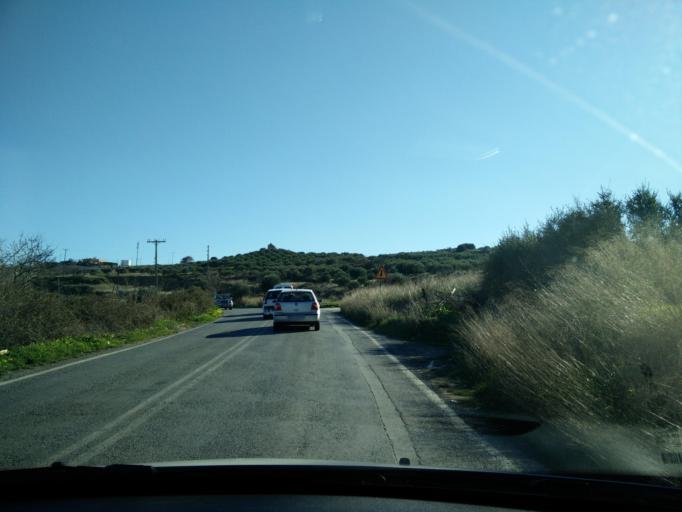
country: GR
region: Crete
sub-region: Nomos Irakleiou
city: Arkalochori
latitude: 35.1368
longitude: 25.2622
